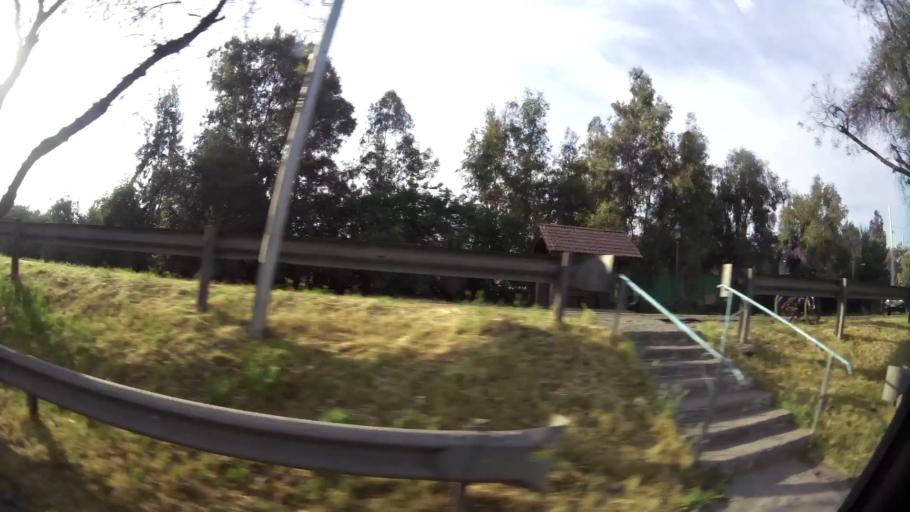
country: CL
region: Santiago Metropolitan
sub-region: Provincia de Talagante
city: Penaflor
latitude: -33.5800
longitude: -70.8273
